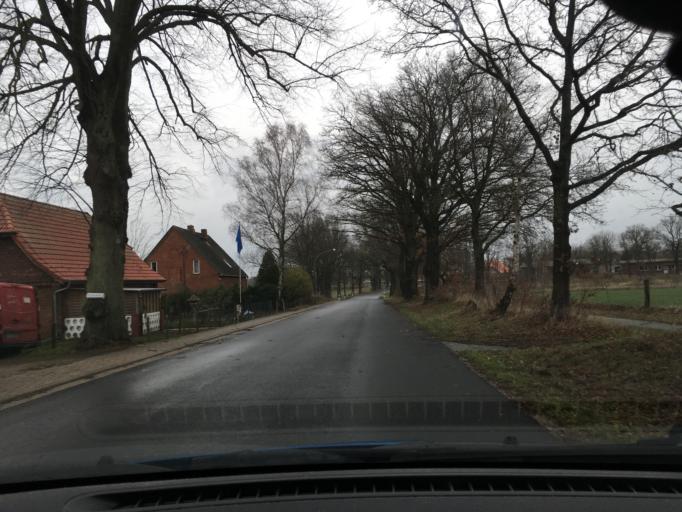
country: DE
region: Schleswig-Holstein
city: Lanze
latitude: 53.3886
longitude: 10.6298
